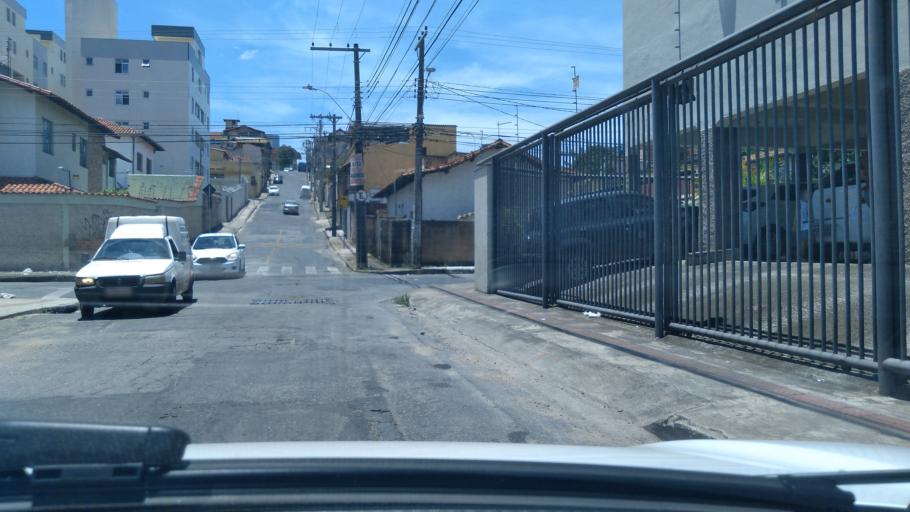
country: BR
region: Minas Gerais
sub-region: Contagem
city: Contagem
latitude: -19.9313
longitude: -43.9976
